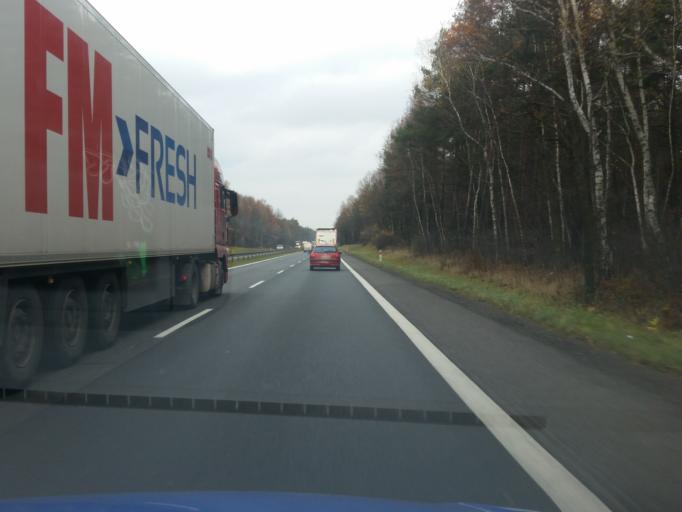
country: PL
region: Silesian Voivodeship
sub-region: Powiat czestochowski
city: Kamienica Polska
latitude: 50.6456
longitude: 19.1347
